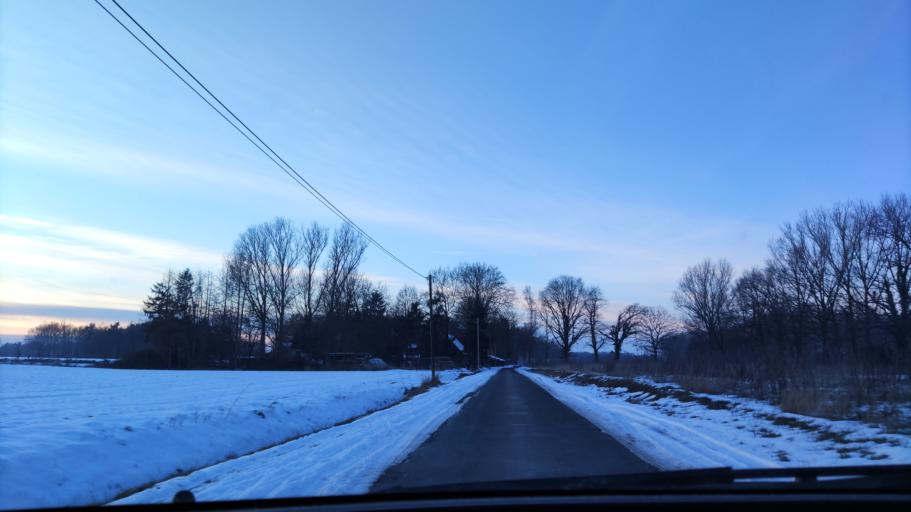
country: DE
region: Lower Saxony
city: Neetze
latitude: 53.2999
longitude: 10.6724
